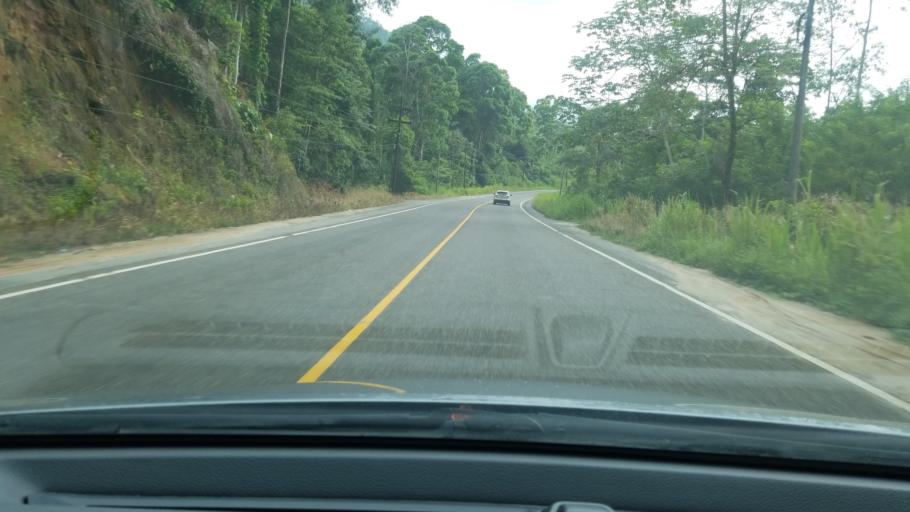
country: HN
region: Cortes
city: Potrerillos
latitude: 15.6075
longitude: -88.2912
